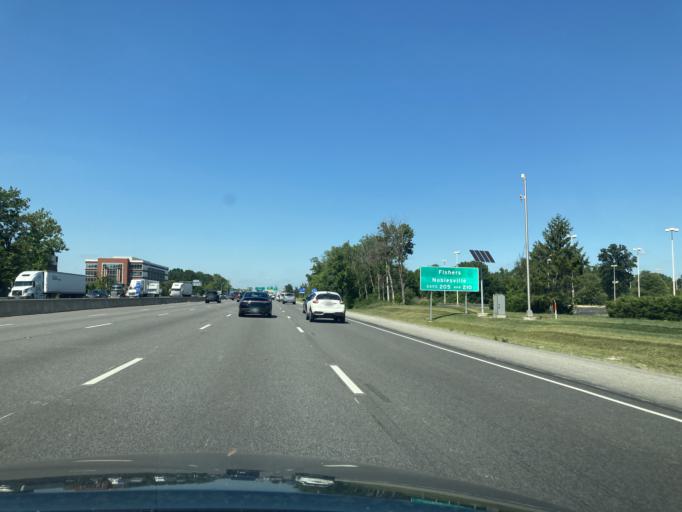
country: US
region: Indiana
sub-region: Hamilton County
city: Fishers
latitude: 39.9331
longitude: -86.0251
